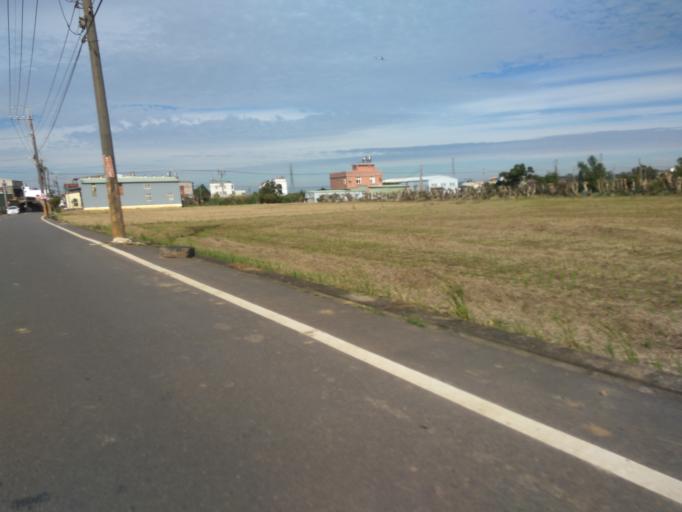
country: TW
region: Taiwan
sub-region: Hsinchu
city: Zhubei
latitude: 24.9528
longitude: 121.1287
